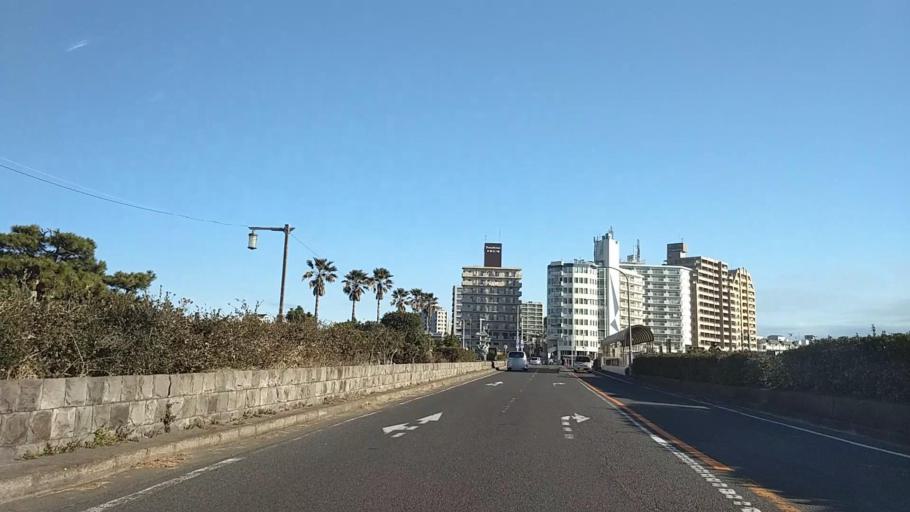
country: JP
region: Kanagawa
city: Fujisawa
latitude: 35.3062
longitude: 139.4831
